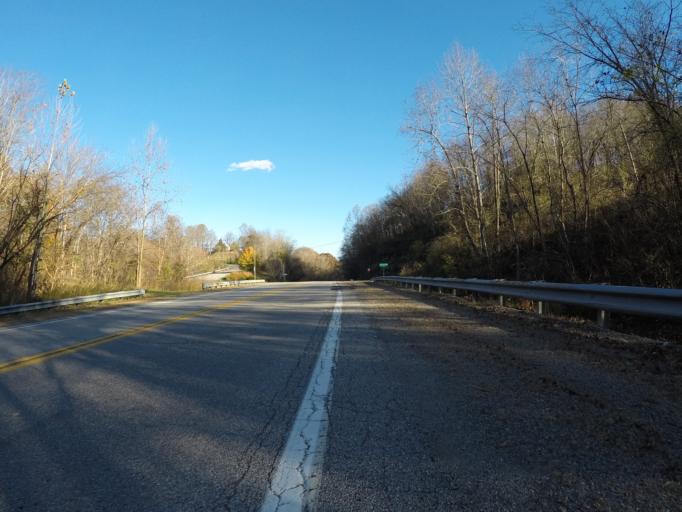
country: US
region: West Virginia
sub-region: Wayne County
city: Ceredo
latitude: 38.3829
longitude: -82.5680
